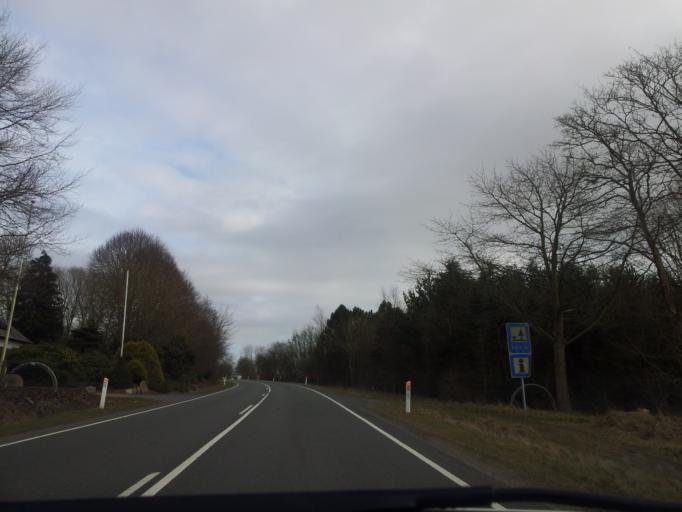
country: DK
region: South Denmark
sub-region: Vejen Kommune
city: Brorup
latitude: 55.4407
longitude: 9.0639
